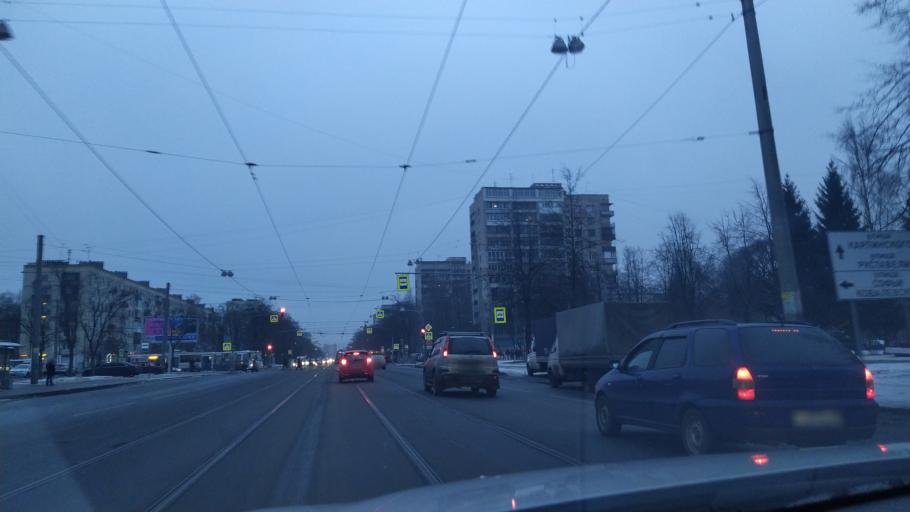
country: RU
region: Leningrad
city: Akademicheskoe
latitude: 60.0108
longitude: 30.4068
